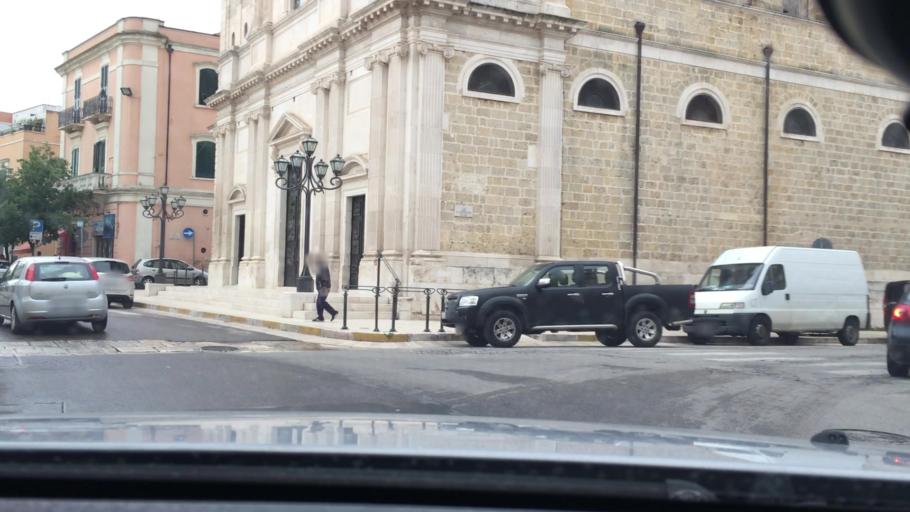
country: IT
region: Apulia
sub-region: Provincia di Bari
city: Gioia del Colle
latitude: 40.8013
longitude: 16.9217
